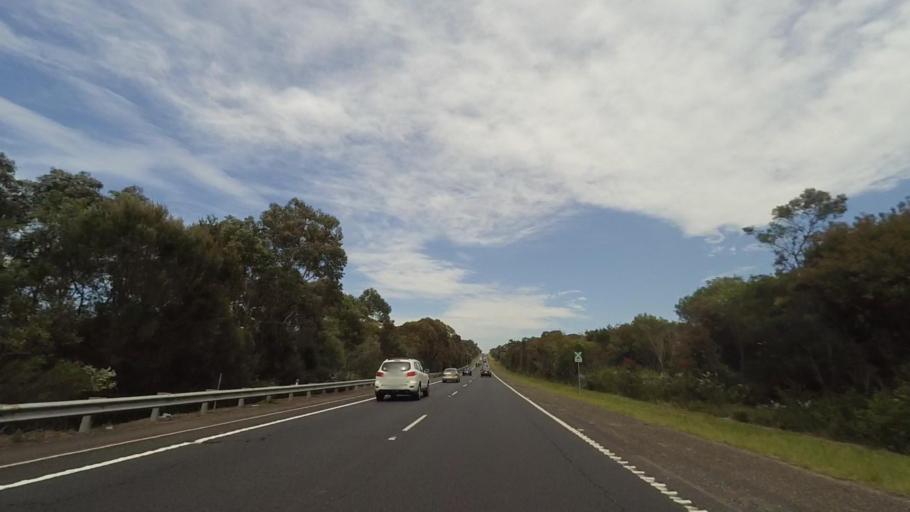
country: AU
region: New South Wales
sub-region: Wollongong
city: Helensburgh
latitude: -34.2159
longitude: 150.9570
